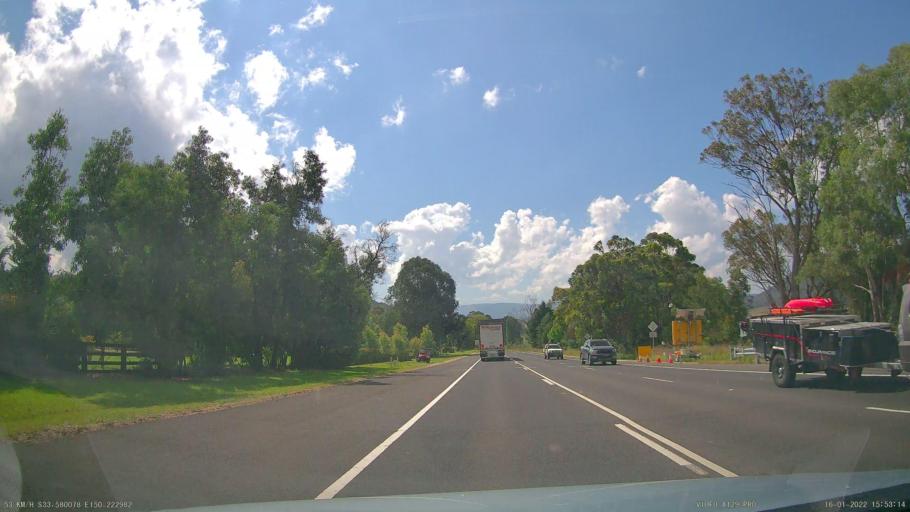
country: AU
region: New South Wales
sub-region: Blue Mountains Municipality
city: Blackheath
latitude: -33.5799
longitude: 150.2228
